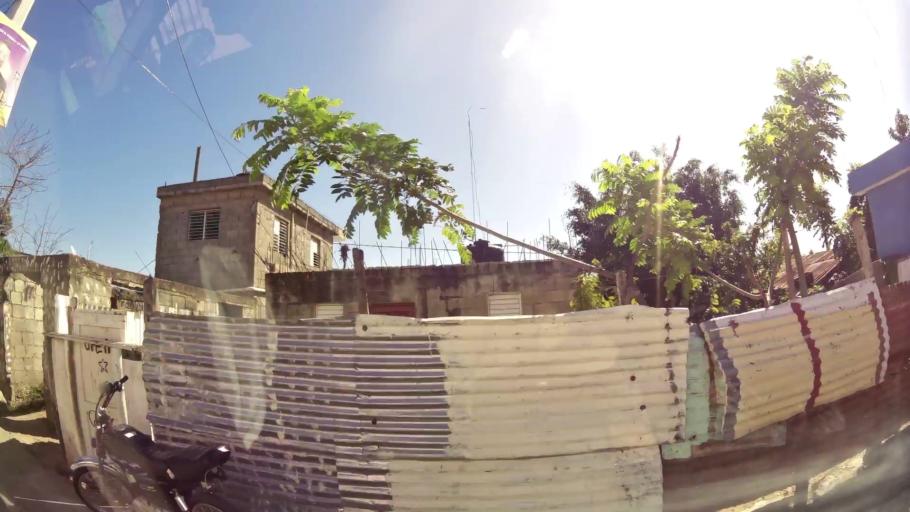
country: DO
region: San Cristobal
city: San Cristobal
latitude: 18.4320
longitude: -70.1168
